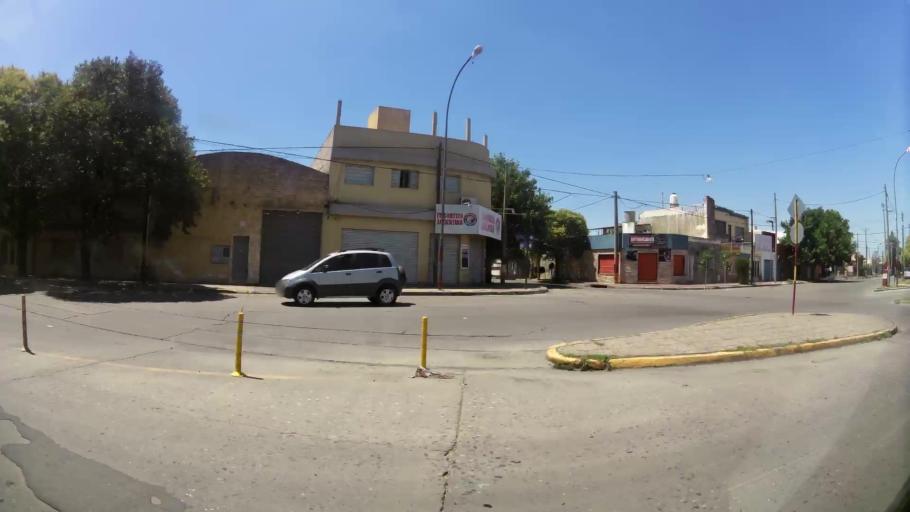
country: AR
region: Cordoba
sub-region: Departamento de Capital
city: Cordoba
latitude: -31.3853
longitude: -64.1950
